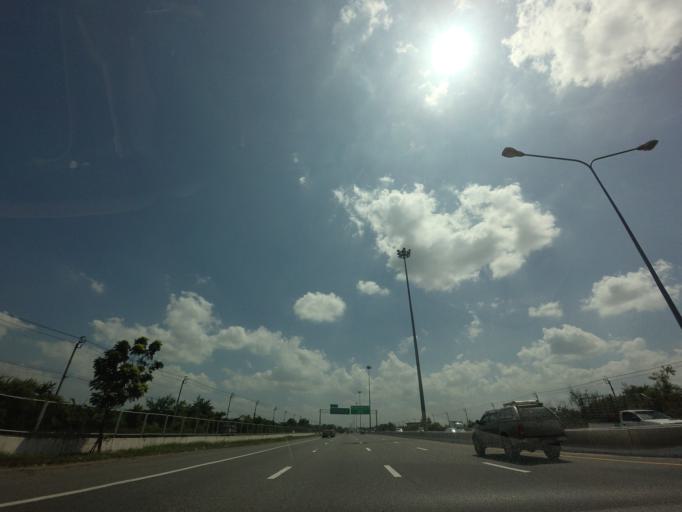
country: TH
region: Bangkok
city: Lat Krabang
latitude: 13.7216
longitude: 100.8146
